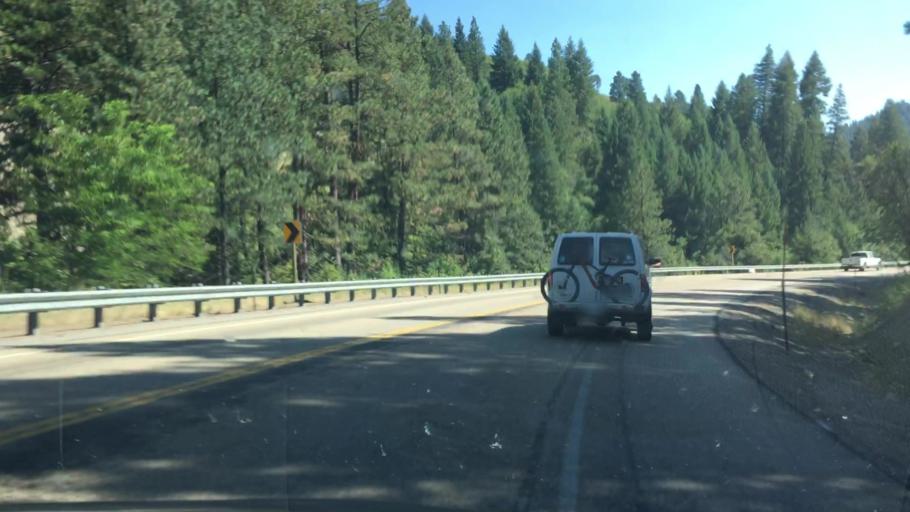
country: US
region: Idaho
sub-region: Valley County
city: Cascade
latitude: 44.1295
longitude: -116.1112
